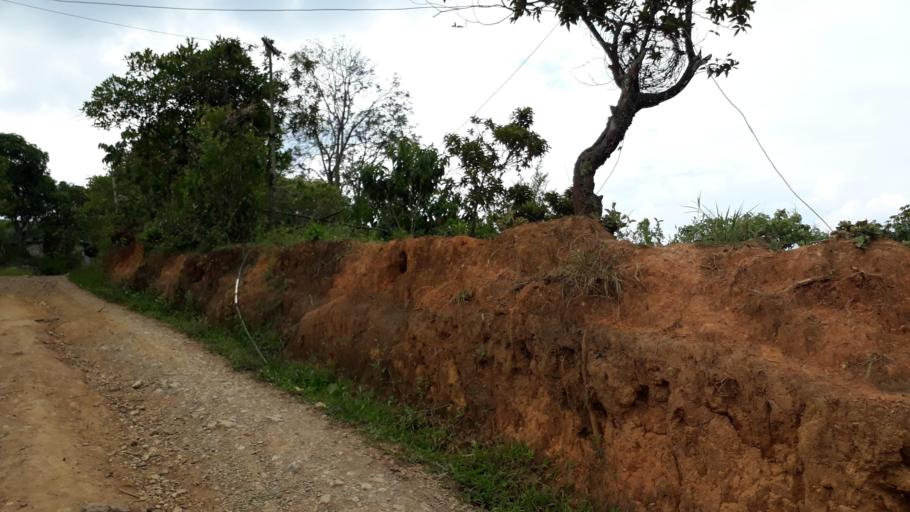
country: CO
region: Valle del Cauca
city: Jamundi
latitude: 3.2237
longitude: -76.6277
